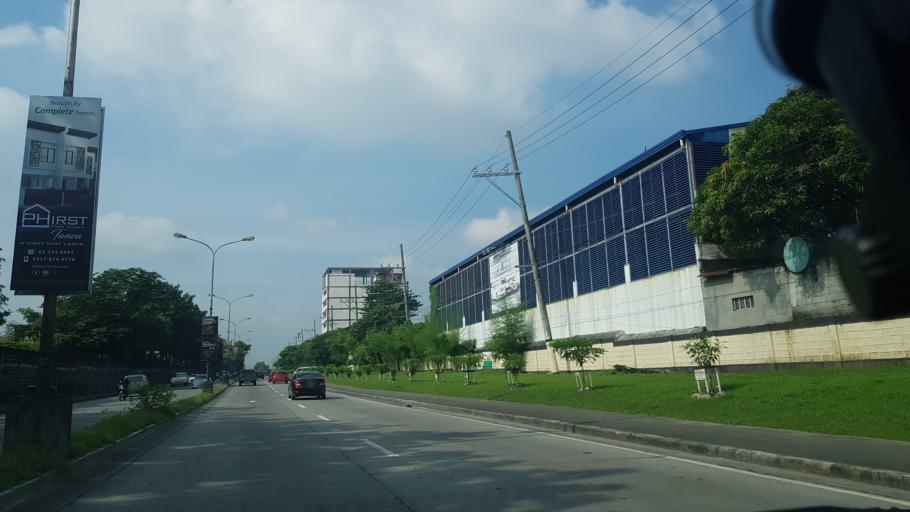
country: PH
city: Sambayanihan People's Village
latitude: 14.4208
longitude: 121.0213
